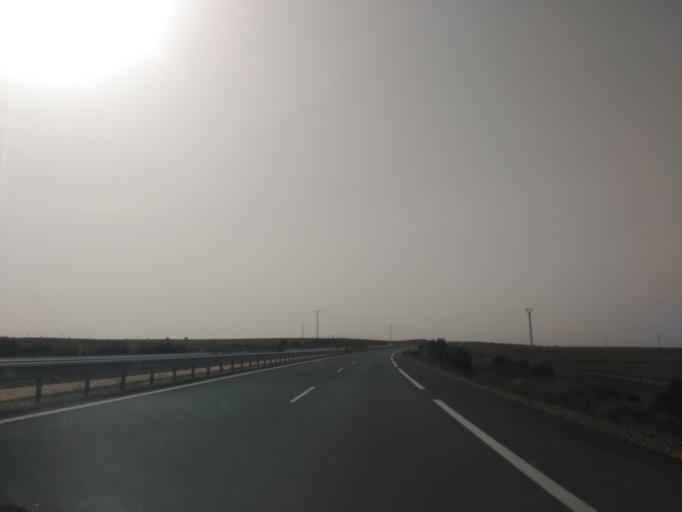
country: ES
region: Castille and Leon
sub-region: Provincia de Palencia
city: Marcilla de Campos
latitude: 42.3315
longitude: -4.3955
